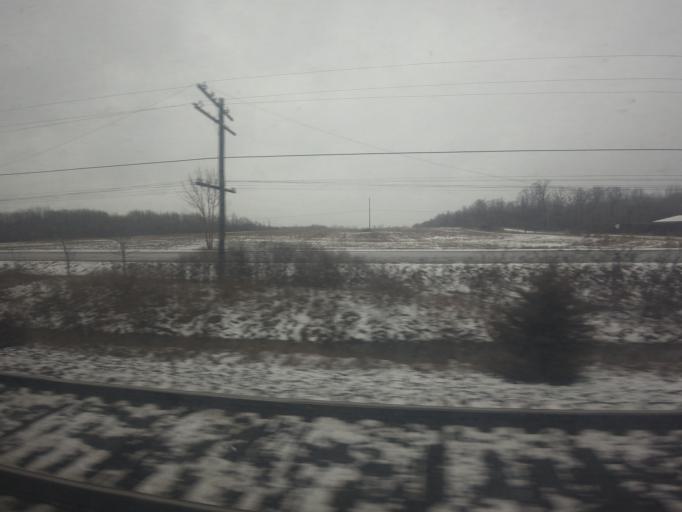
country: CA
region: Ontario
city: Belleville
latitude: 44.1570
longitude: -77.4549
